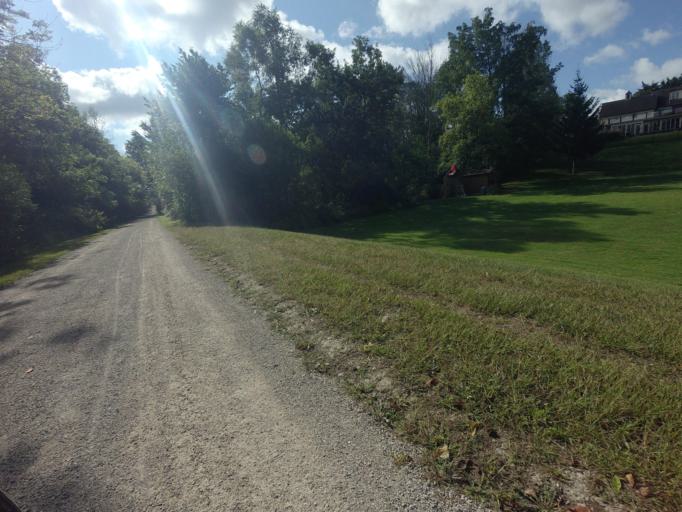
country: CA
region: Ontario
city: Huron East
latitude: 43.7354
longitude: -81.4213
